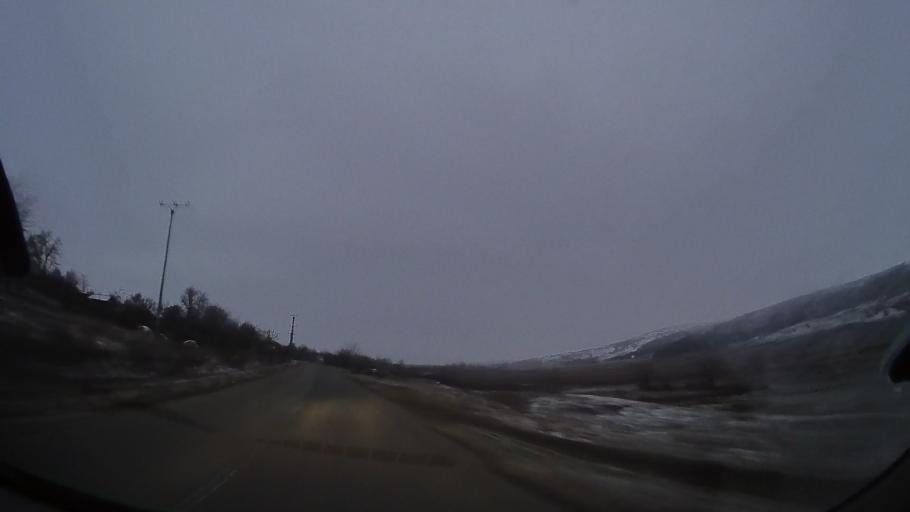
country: RO
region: Vaslui
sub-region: Comuna Vutcani
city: Vutcani
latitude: 46.4082
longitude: 27.9942
